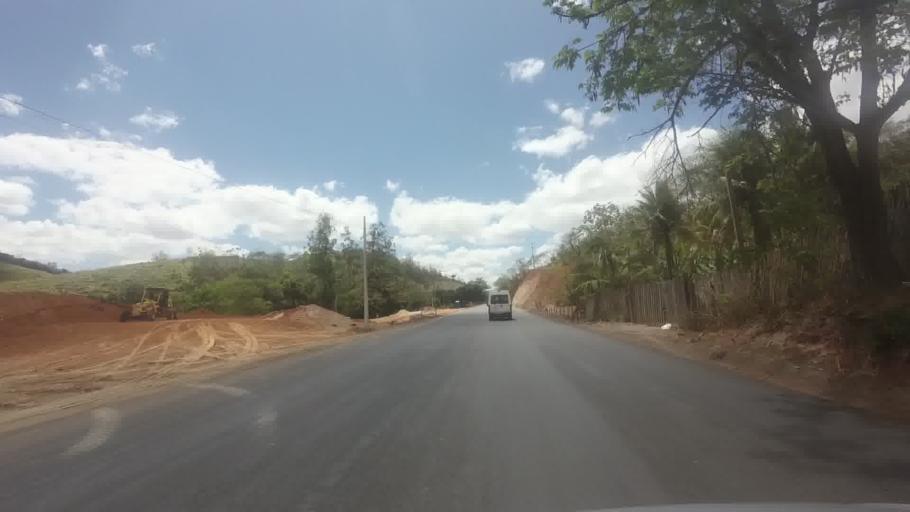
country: BR
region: Rio de Janeiro
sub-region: Santo Antonio De Padua
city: Santo Antonio de Padua
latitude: -21.5055
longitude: -42.0827
